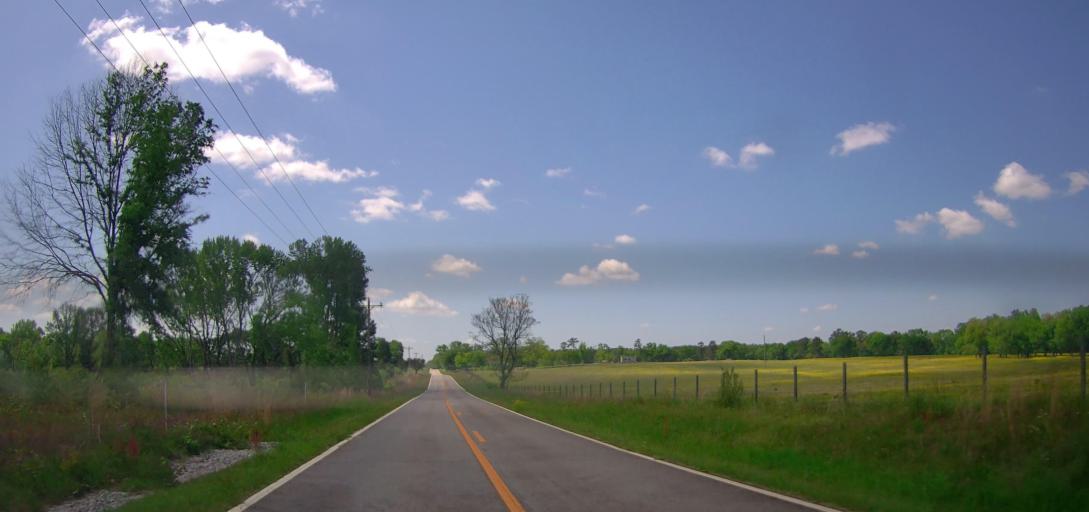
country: US
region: Georgia
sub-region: Putnam County
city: Eatonton
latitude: 33.3282
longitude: -83.3152
